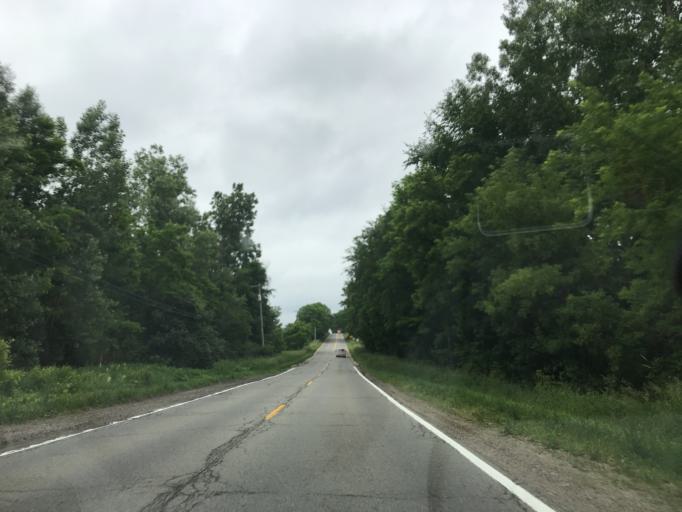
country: US
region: Michigan
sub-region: Oakland County
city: South Lyon
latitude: 42.5079
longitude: -83.6594
